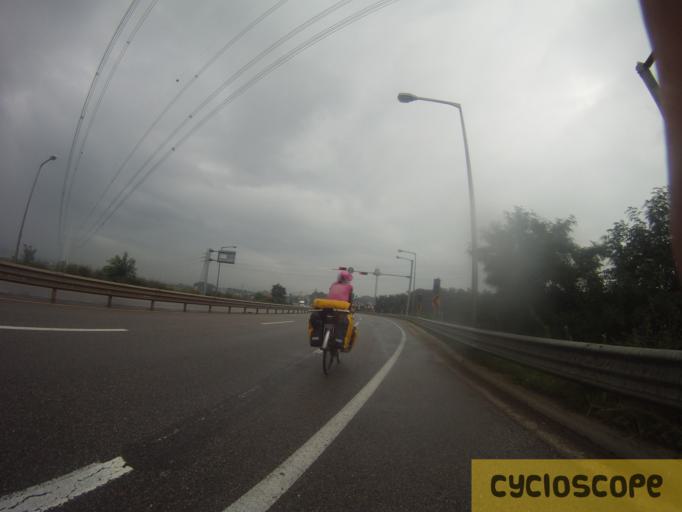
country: KR
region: Gyeonggi-do
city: Hwaseong-si
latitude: 37.1262
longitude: 126.8578
